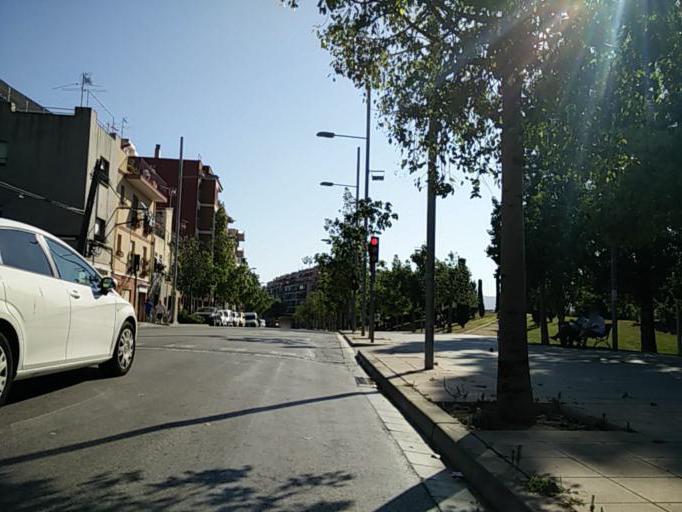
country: ES
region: Catalonia
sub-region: Provincia de Barcelona
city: Llefia
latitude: 41.4531
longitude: 2.2256
